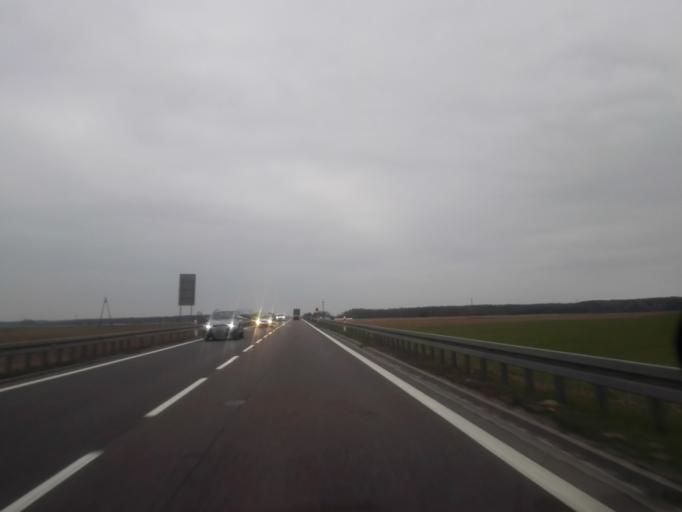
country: PL
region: Podlasie
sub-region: Powiat grajewski
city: Szczuczyn
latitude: 53.4967
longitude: 22.2290
